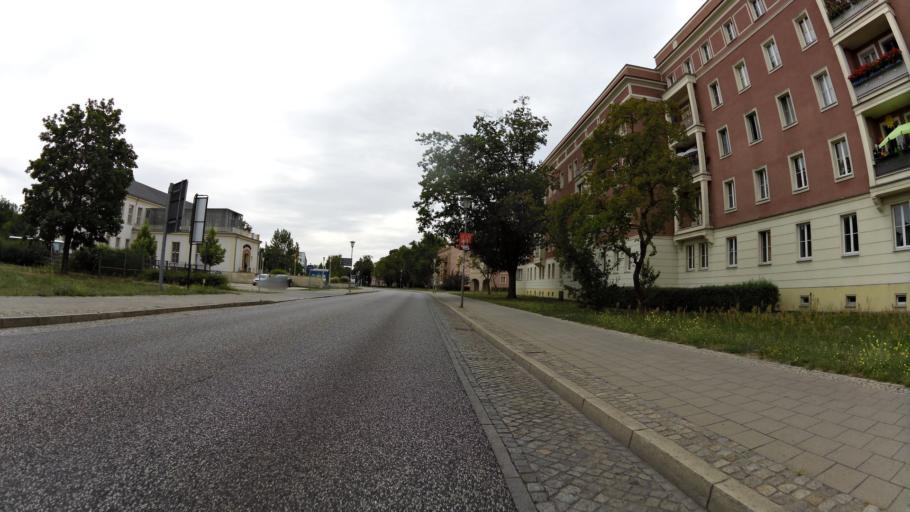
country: DE
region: Brandenburg
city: Eisenhuettenstadt
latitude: 52.1440
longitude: 14.6345
